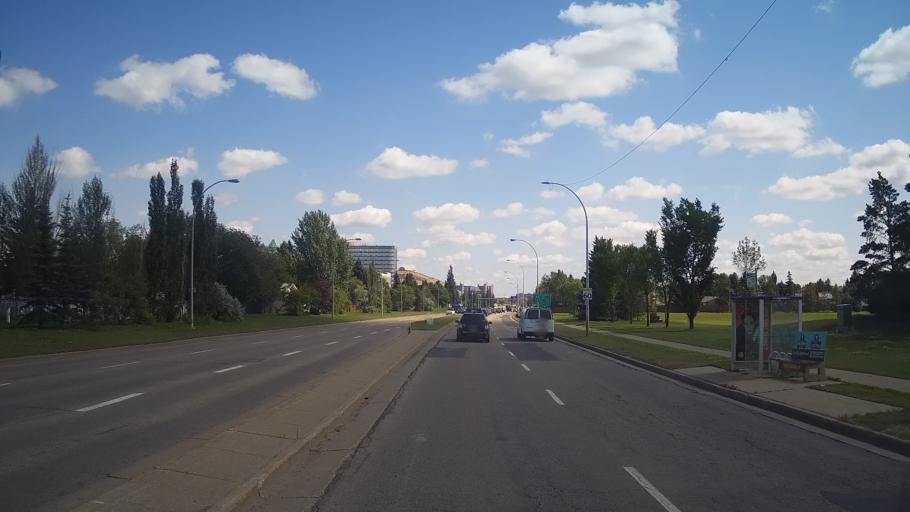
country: CA
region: Alberta
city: St. Albert
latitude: 53.5216
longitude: -113.6370
